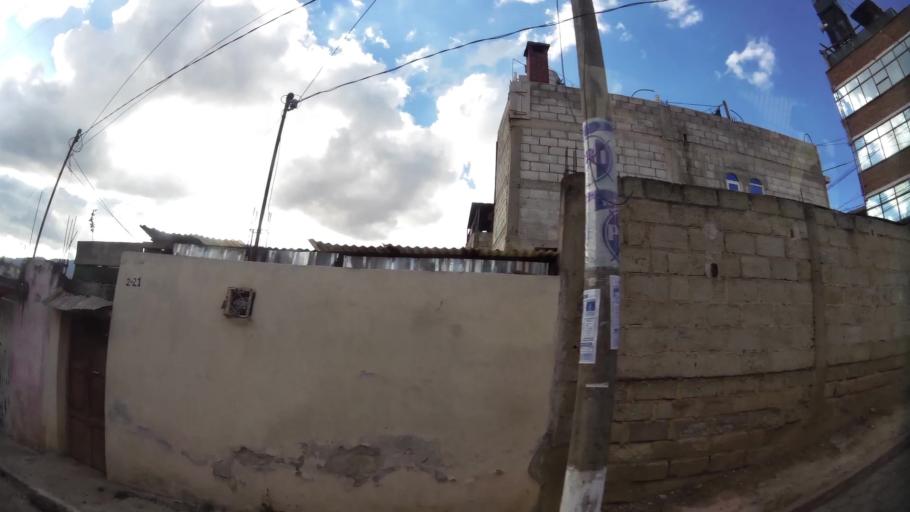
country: GT
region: Quetzaltenango
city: Quetzaltenango
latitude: 14.8520
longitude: -91.5167
